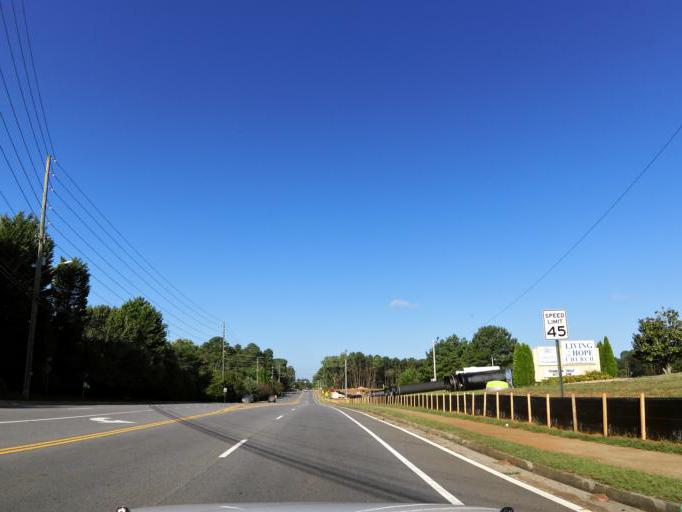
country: US
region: Georgia
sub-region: Cobb County
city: Kennesaw
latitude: 33.9983
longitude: -84.6493
